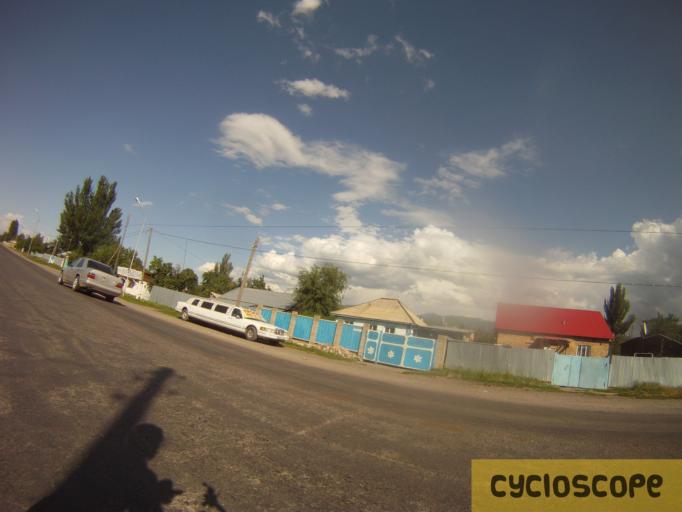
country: KZ
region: Almaty Oblysy
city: Turgen'
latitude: 43.3907
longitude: 77.5810
